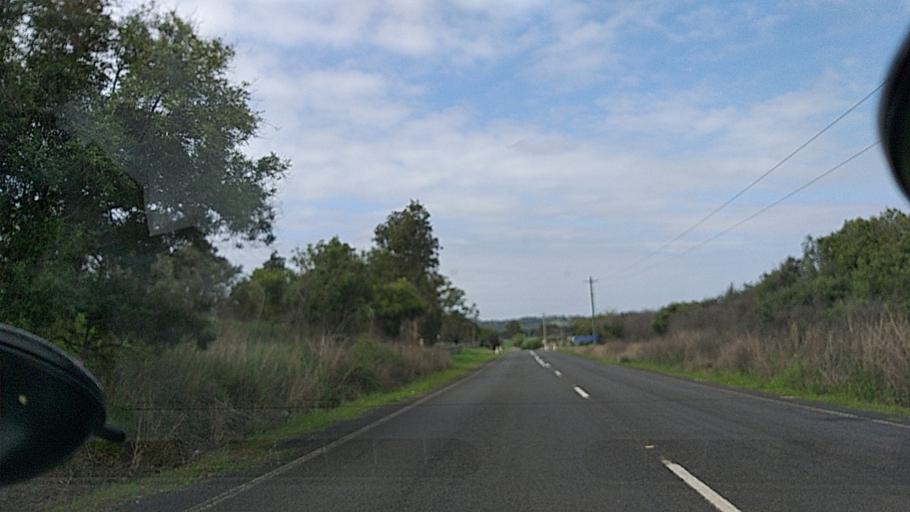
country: AU
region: New South Wales
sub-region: Camden
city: Camden South
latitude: -34.1261
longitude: 150.7225
